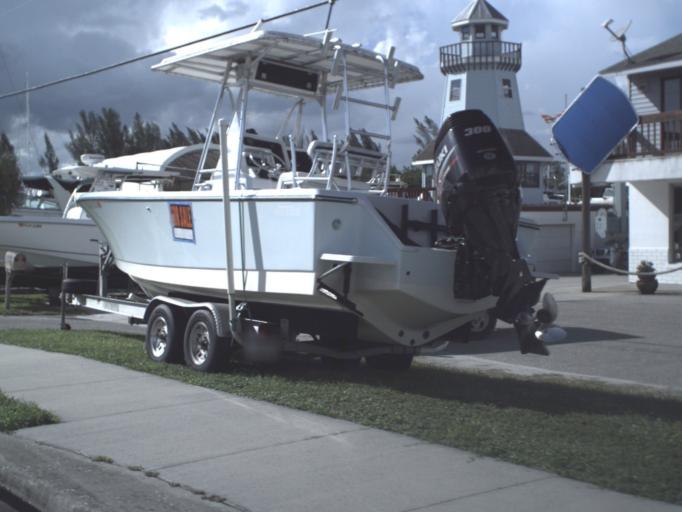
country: US
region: Florida
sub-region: Charlotte County
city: Punta Gorda
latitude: 26.9430
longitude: -82.0365
